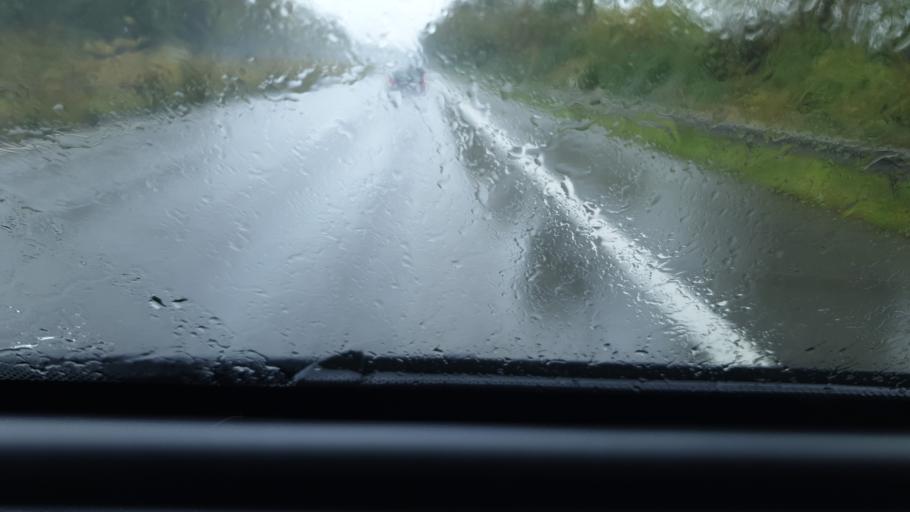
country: DE
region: North Rhine-Westphalia
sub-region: Regierungsbezirk Koln
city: Alsdorf
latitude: 50.8411
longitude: 6.1932
